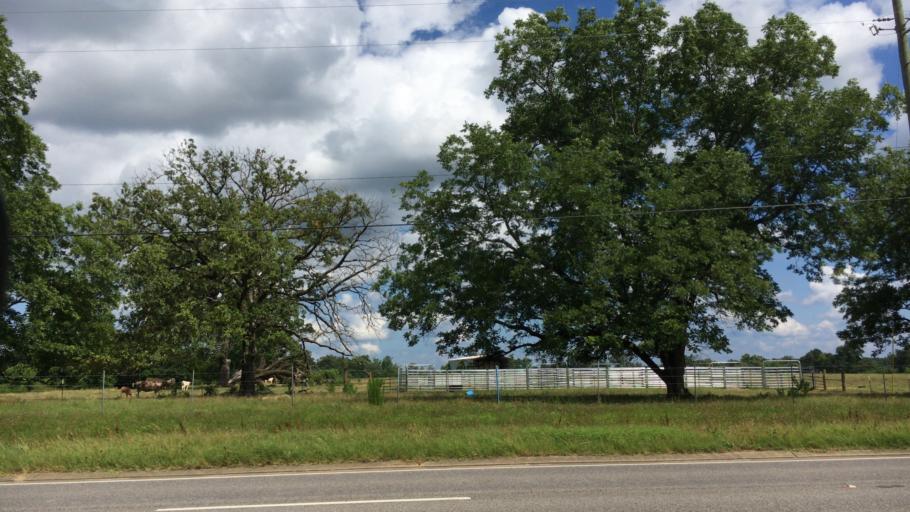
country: US
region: Louisiana
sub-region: Lincoln Parish
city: Ruston
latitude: 32.4932
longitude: -92.6390
